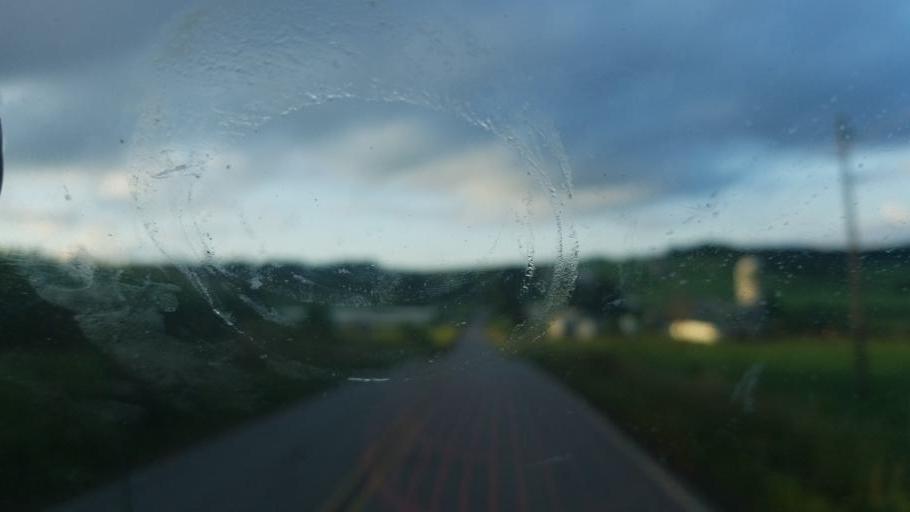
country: US
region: Pennsylvania
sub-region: Potter County
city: Galeton
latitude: 41.8897
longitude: -77.7617
